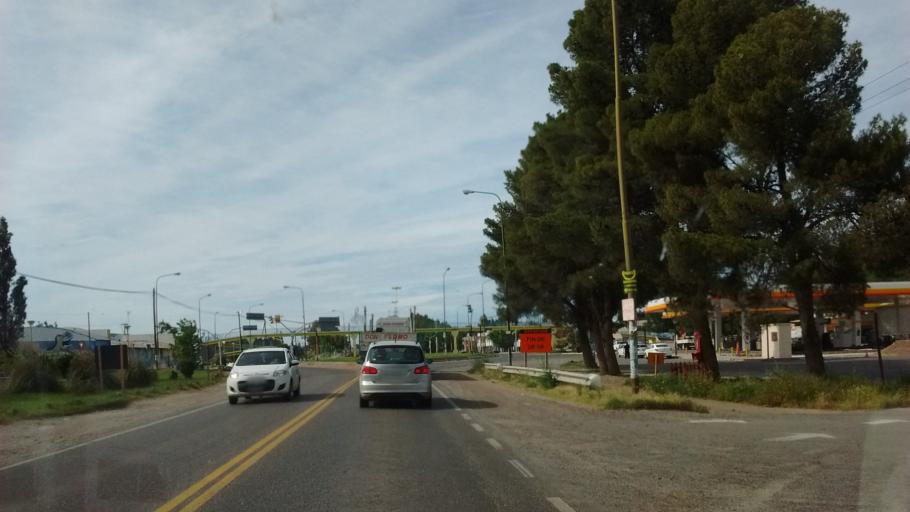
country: AR
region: Neuquen
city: Centenario
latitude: -38.8272
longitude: -68.1314
